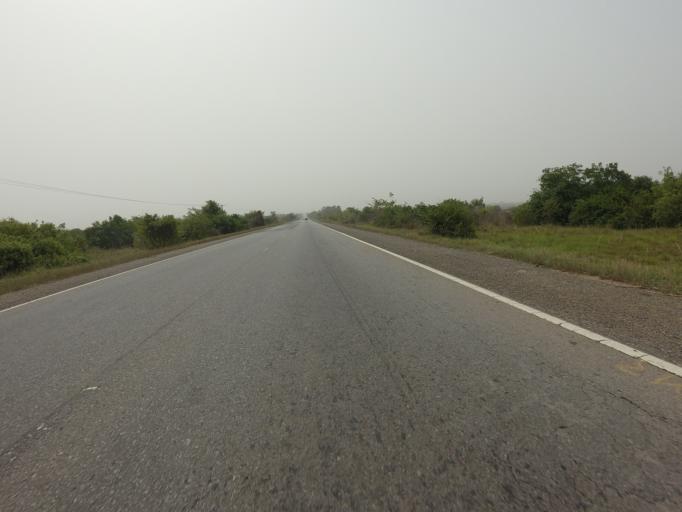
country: GH
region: Volta
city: Anloga
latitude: 5.9620
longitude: 0.5244
